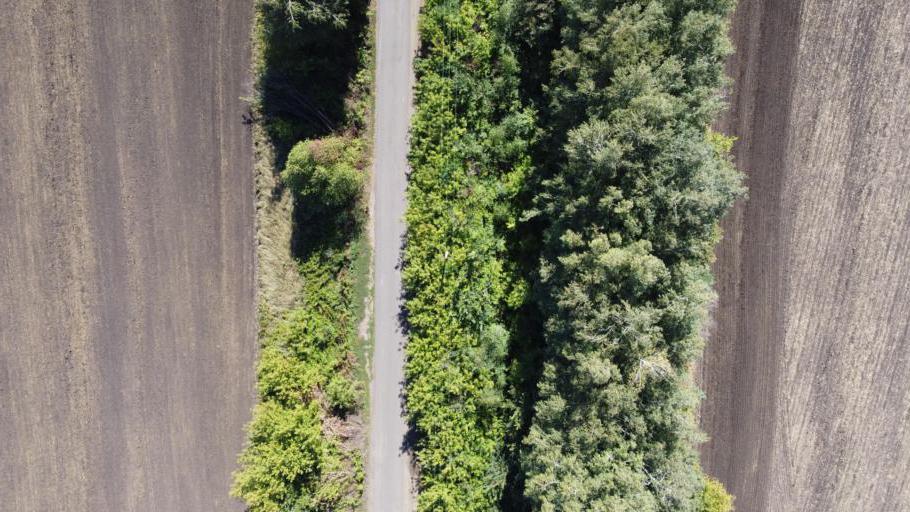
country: RU
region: Kursk
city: Kshenskiy
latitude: 51.8672
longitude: 37.6861
